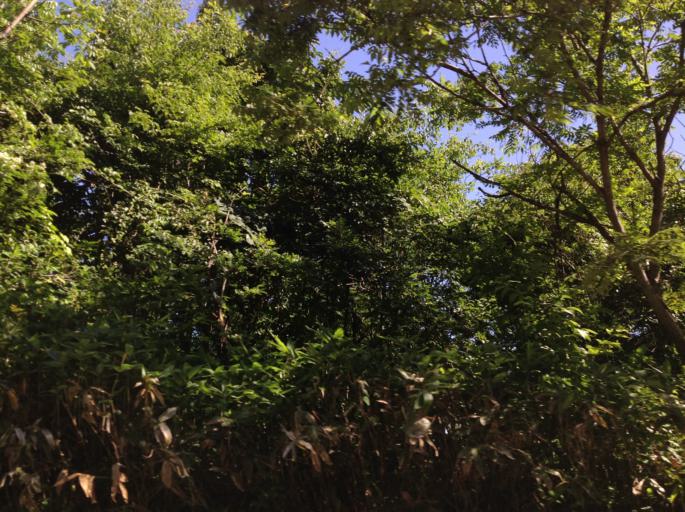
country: JP
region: Akita
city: Kakunodatemachi
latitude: 39.6976
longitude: 140.6501
